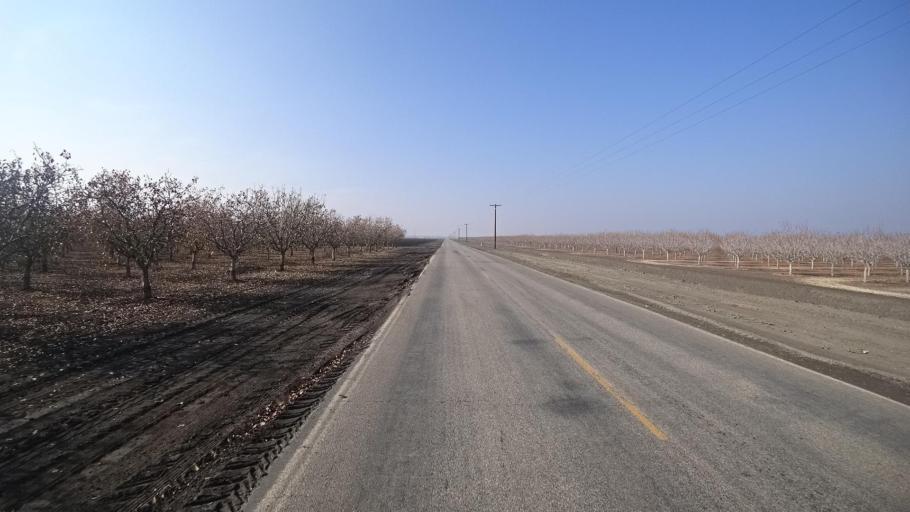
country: US
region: California
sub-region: Kern County
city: Buttonwillow
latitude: 35.3545
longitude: -119.4381
